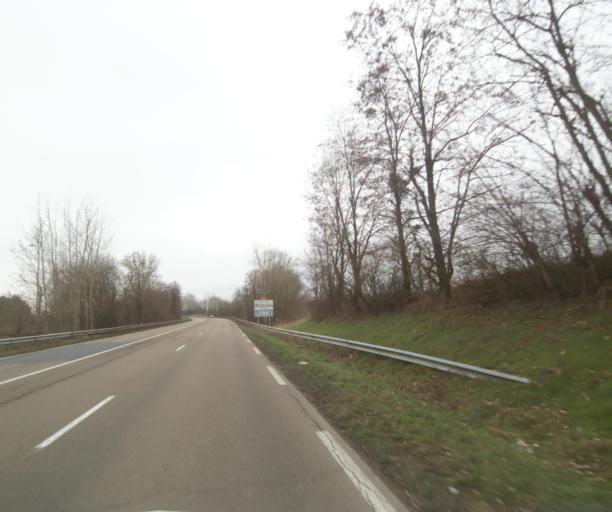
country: FR
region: Champagne-Ardenne
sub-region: Departement de la Haute-Marne
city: Bienville
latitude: 48.5873
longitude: 5.0293
